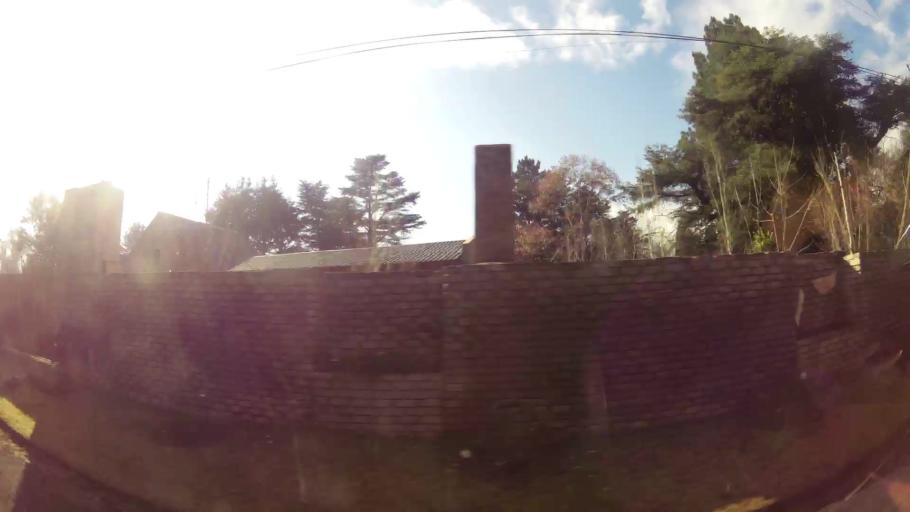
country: ZA
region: Gauteng
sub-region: Sedibeng District Municipality
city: Meyerton
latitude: -26.5466
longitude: 28.0632
